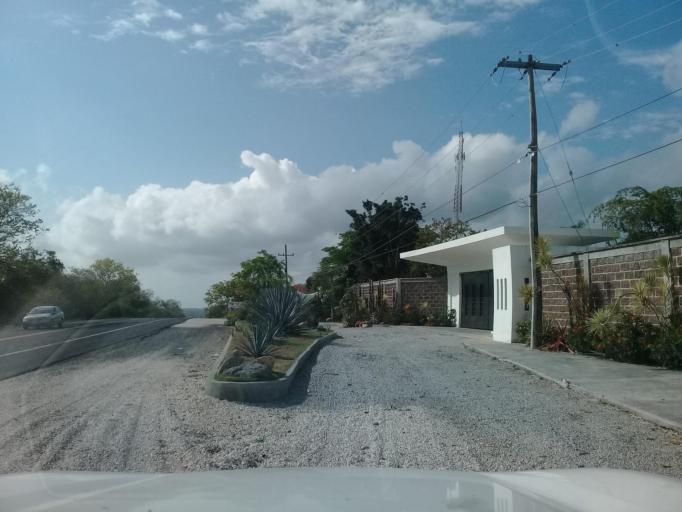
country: MX
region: Veracruz
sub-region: Emiliano Zapata
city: Plan del Rio
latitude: 19.4124
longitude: -96.6523
